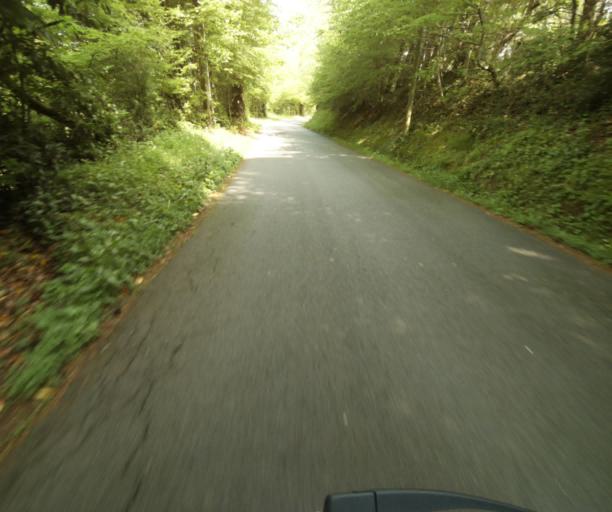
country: FR
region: Limousin
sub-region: Departement de la Correze
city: Tulle
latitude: 45.2741
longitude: 1.7611
